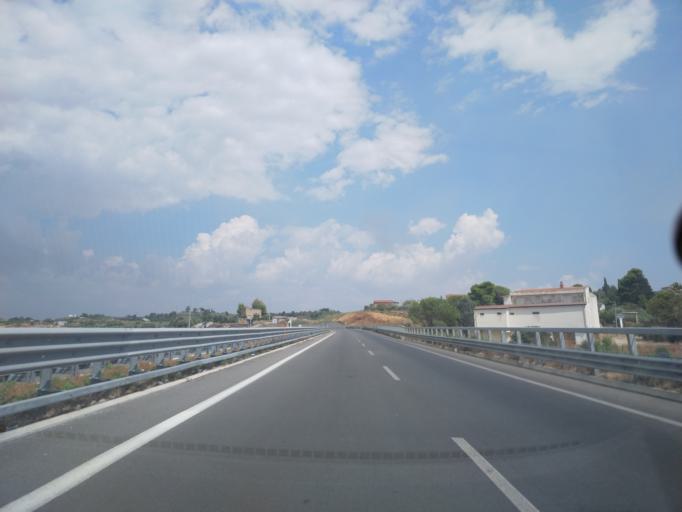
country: IT
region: Sicily
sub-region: Agrigento
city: Grotte
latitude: 37.3606
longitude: 13.6950
